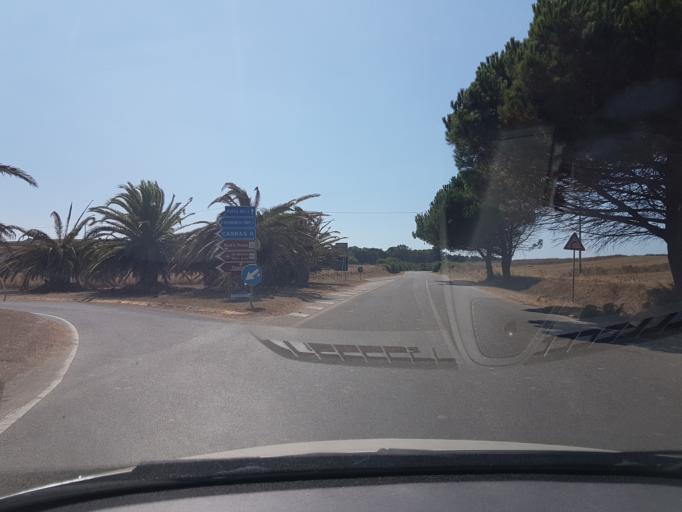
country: IT
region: Sardinia
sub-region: Provincia di Oristano
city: Nurachi
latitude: 39.9851
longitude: 8.4546
